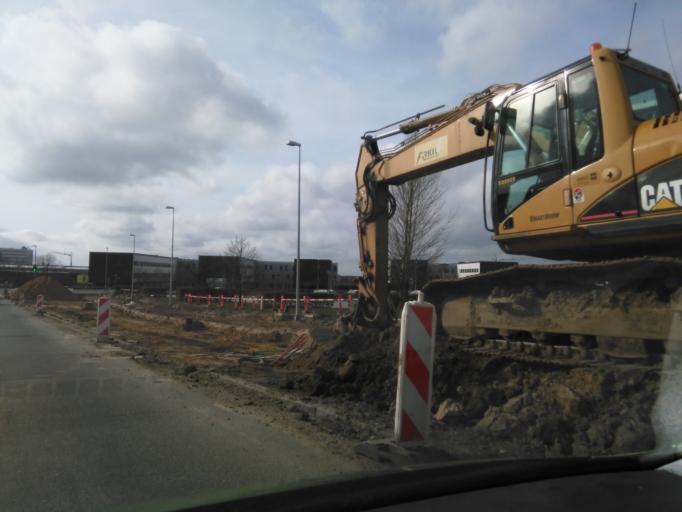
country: DK
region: Central Jutland
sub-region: Arhus Kommune
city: Arhus
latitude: 56.1900
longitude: 10.1814
